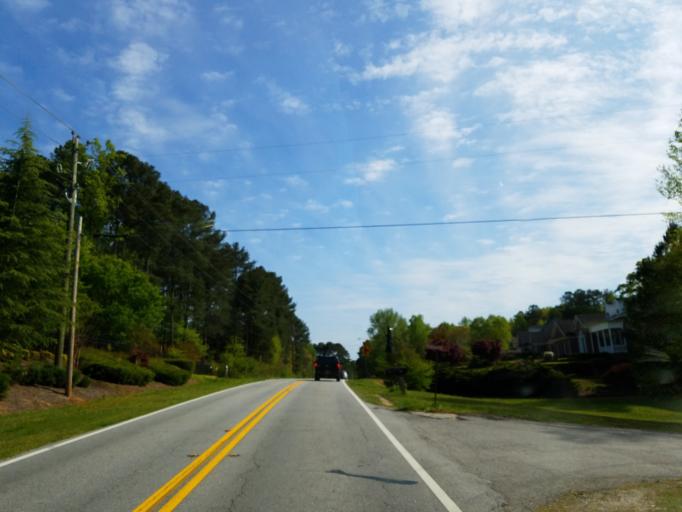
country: US
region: Georgia
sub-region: Douglas County
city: Lithia Springs
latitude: 33.7676
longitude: -84.6367
